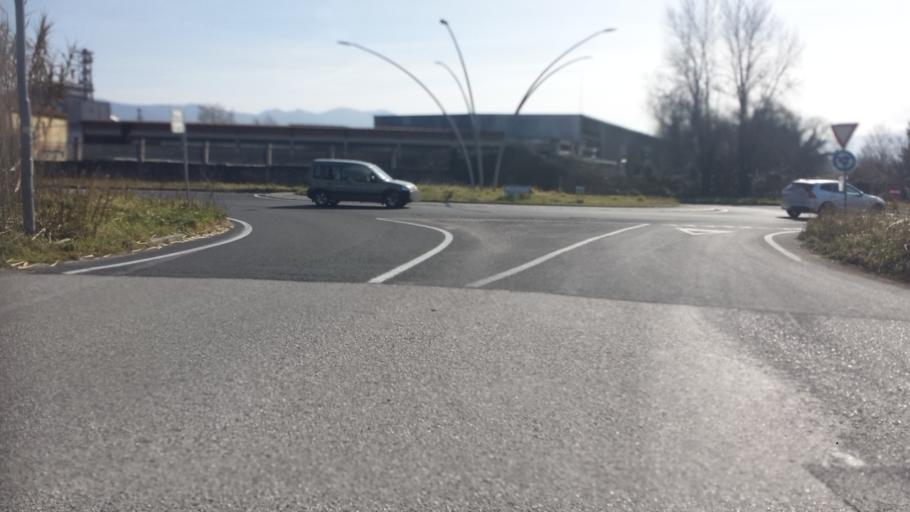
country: IT
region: Umbria
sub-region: Provincia di Terni
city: Terni
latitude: 42.5673
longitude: 12.5978
